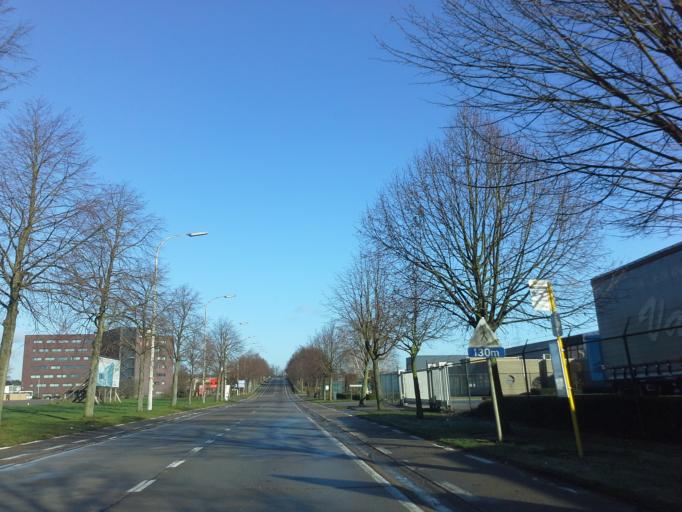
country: BE
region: Flanders
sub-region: Provincie Antwerpen
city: Herenthout
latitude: 51.1613
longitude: 4.7889
